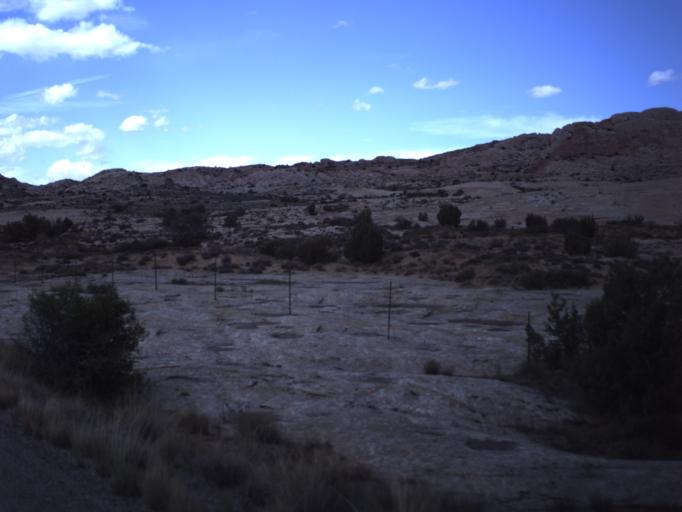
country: US
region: Utah
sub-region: San Juan County
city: Blanding
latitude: 37.2613
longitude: -109.6631
